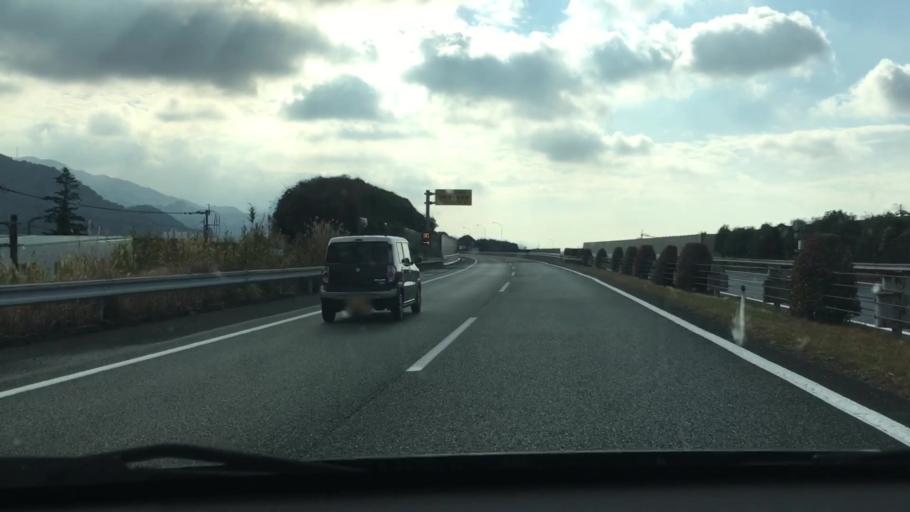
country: JP
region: Kumamoto
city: Yatsushiro
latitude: 32.5180
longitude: 130.6514
